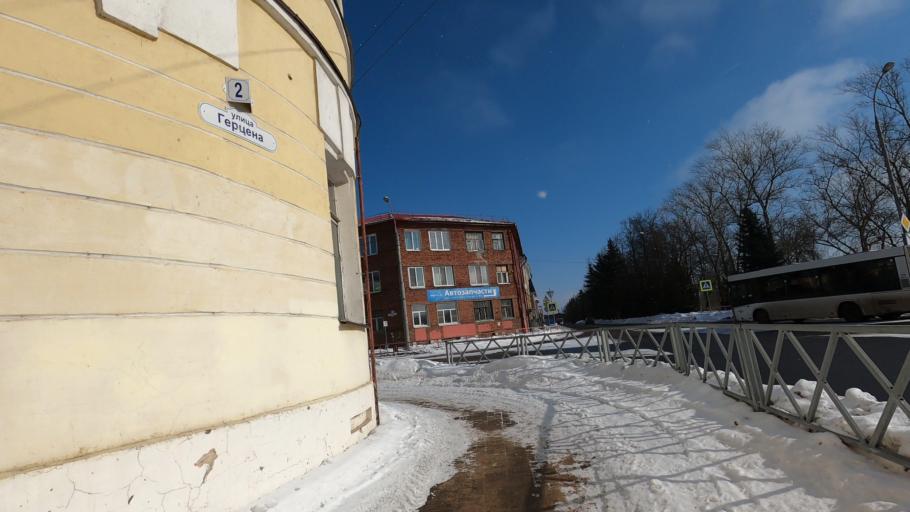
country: RU
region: Jaroslavl
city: Rybinsk
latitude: 58.0465
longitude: 38.8529
